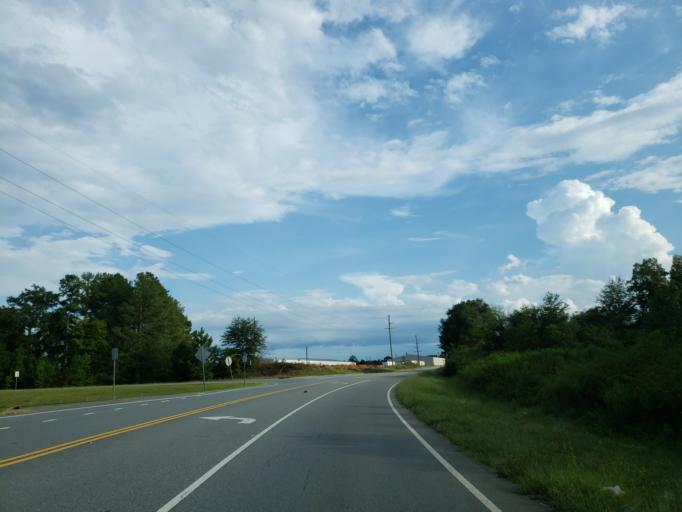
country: US
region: Georgia
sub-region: Bartow County
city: Euharlee
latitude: 34.1163
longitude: -84.9264
